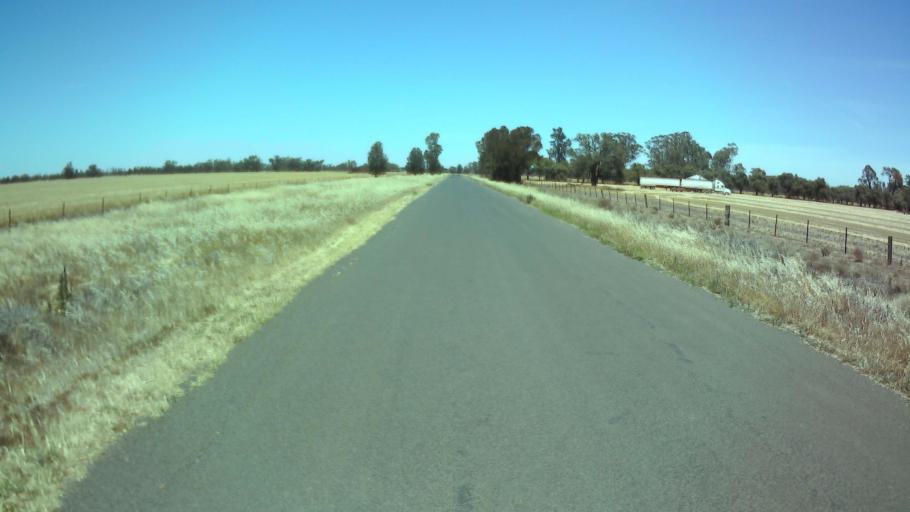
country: AU
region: New South Wales
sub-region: Weddin
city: Grenfell
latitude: -34.0292
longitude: 147.7910
